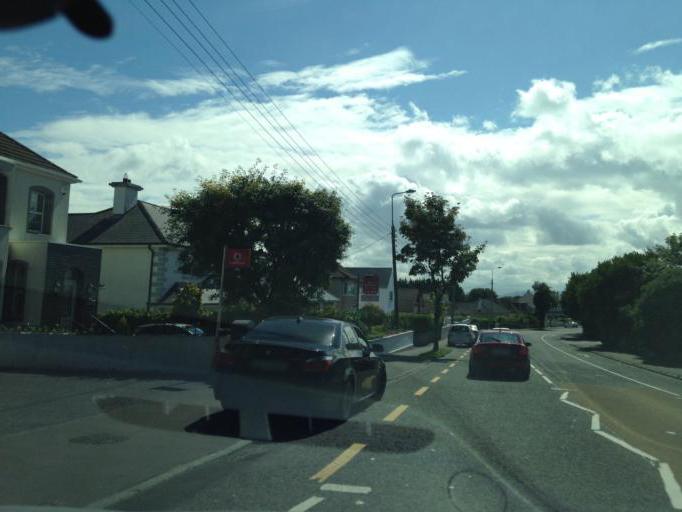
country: IE
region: Connaught
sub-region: County Galway
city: Gaillimh
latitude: 53.2657
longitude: -9.0881
